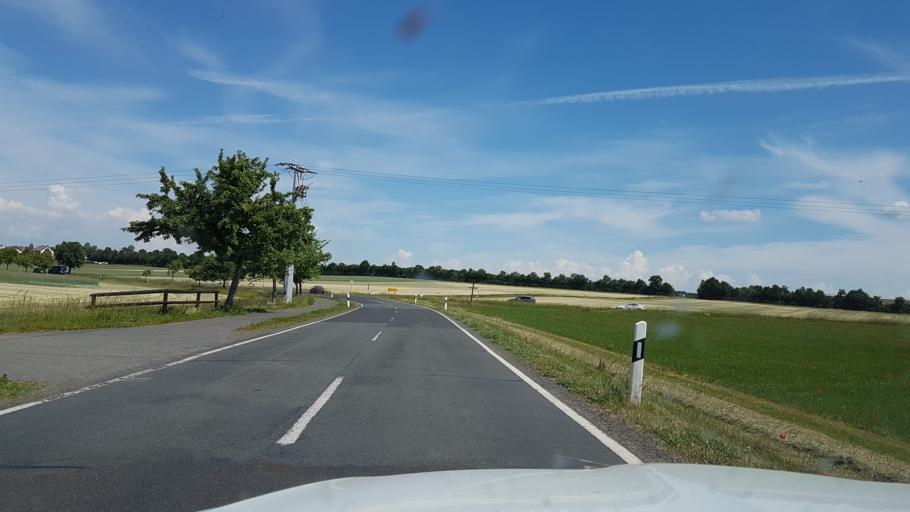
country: DE
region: Bavaria
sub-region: Regierungsbezirk Unterfranken
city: Knetzgau
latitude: 49.9928
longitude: 10.5081
